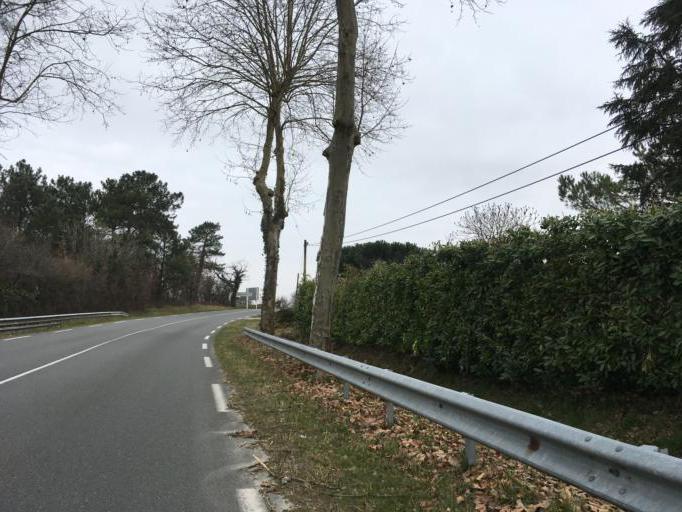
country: FR
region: Poitou-Charentes
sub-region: Departement de la Charente-Maritime
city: Mirambeau
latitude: 45.3303
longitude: -0.5779
